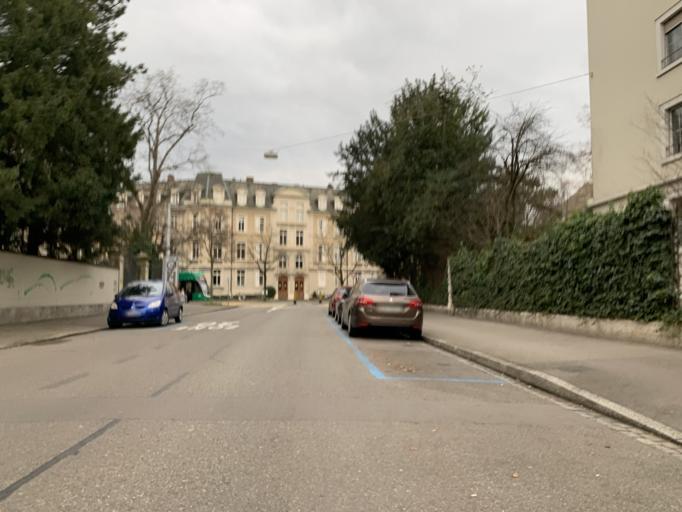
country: CH
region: Basel-Landschaft
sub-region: Bezirk Arlesheim
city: Birsfelden
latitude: 47.5512
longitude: 7.6044
